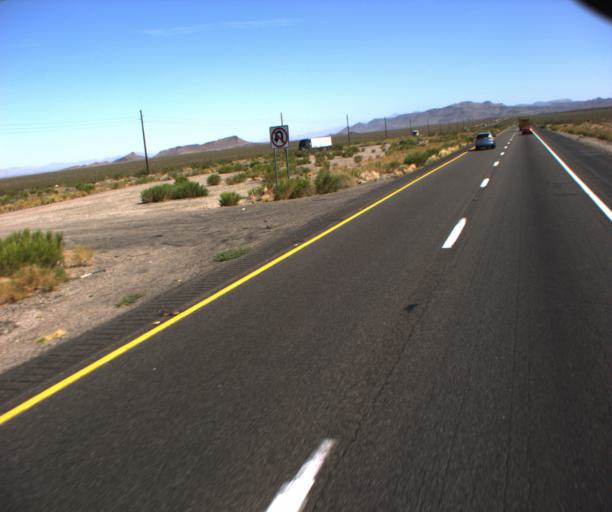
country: US
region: Arizona
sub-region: Mohave County
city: Kingman
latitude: 35.0762
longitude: -114.1221
